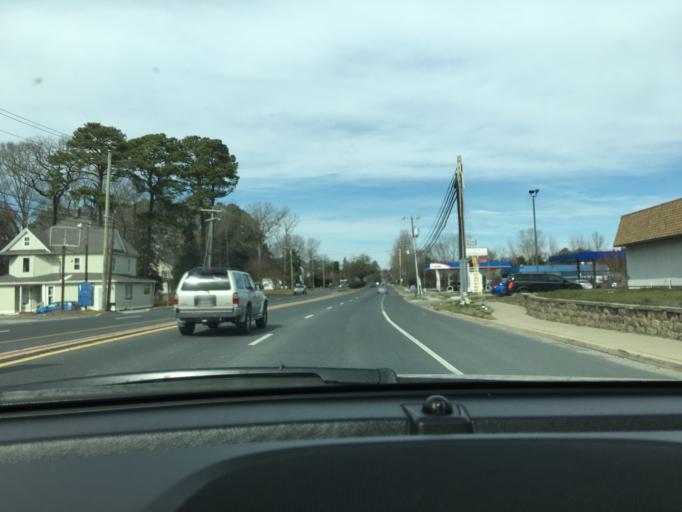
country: US
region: Maryland
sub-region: Wicomico County
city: Salisbury
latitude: 38.3706
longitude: -75.6149
